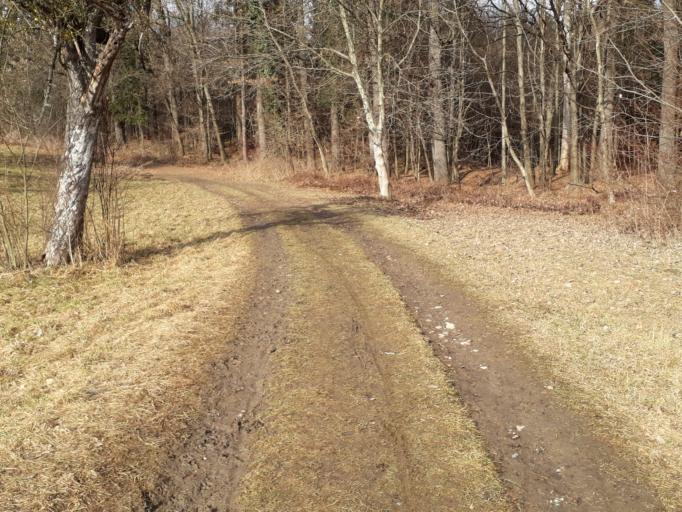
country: AT
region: Styria
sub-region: Politischer Bezirk Graz-Umgebung
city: Stattegg
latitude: 47.1173
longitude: 15.4193
